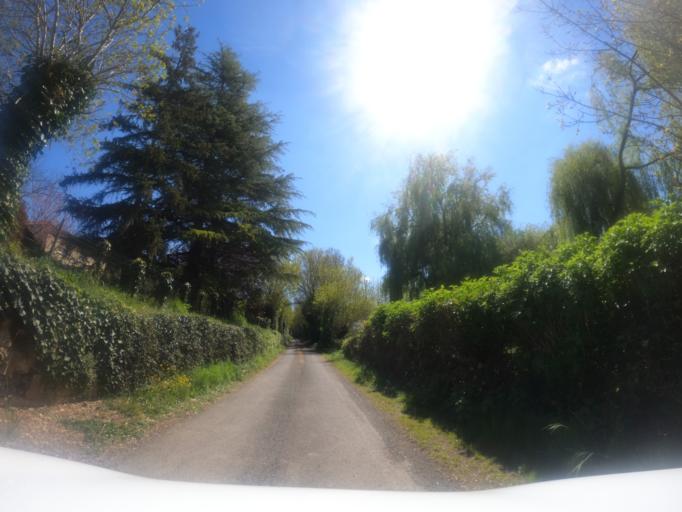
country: FR
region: Pays de la Loire
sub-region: Departement de la Vendee
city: Fontenay-le-Comte
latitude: 46.4342
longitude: -0.8733
